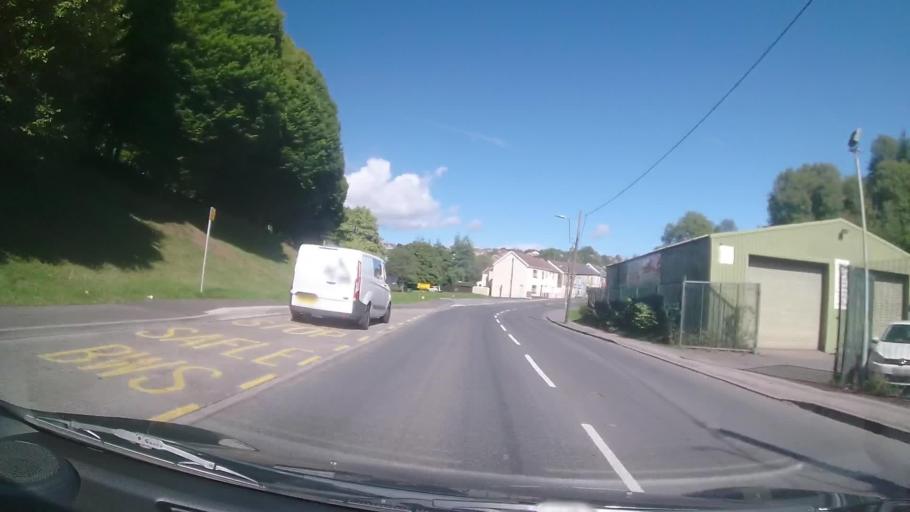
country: GB
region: Wales
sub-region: Merthyr Tydfil County Borough
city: Merthyr Tydfil
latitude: 51.7577
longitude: -3.3634
